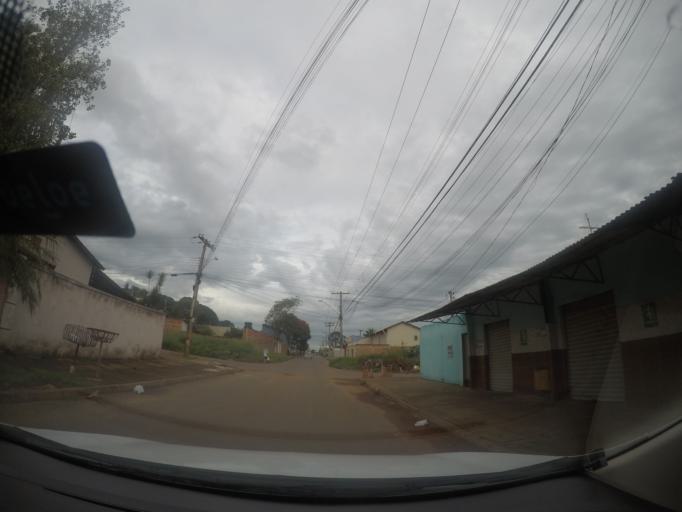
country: BR
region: Goias
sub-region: Goiania
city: Goiania
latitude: -16.5968
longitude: -49.3066
